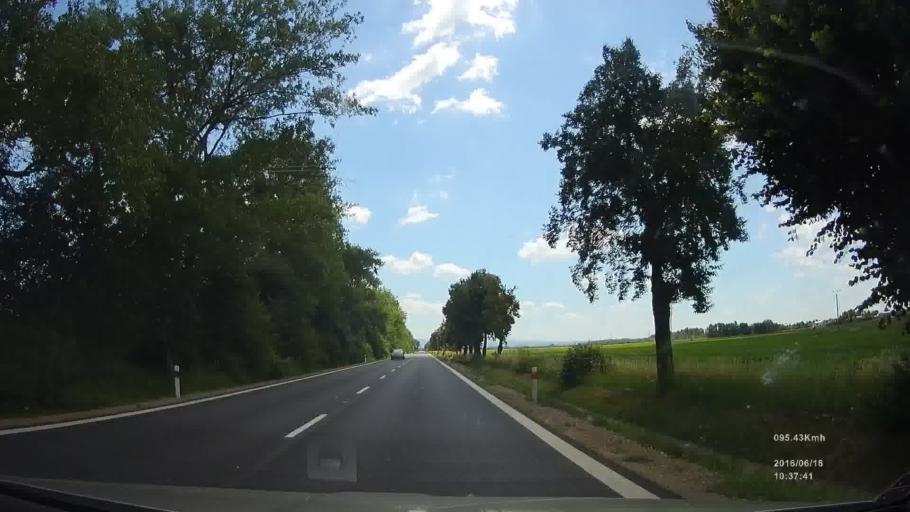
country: SK
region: Kosicky
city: Sobrance
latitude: 48.7629
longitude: 22.1116
